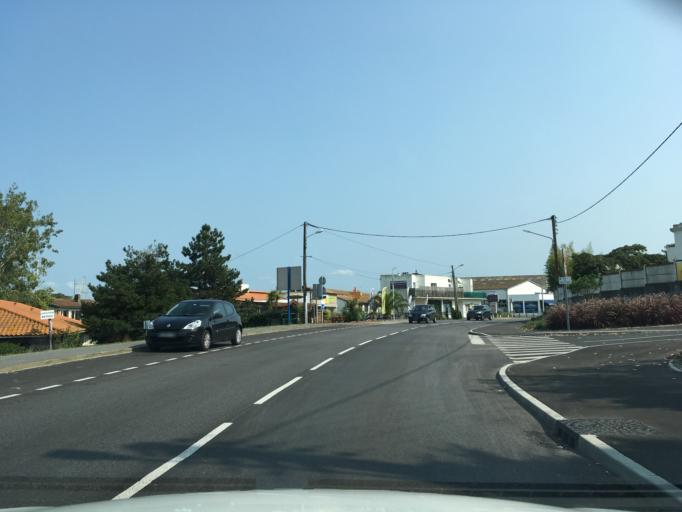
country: FR
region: Aquitaine
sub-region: Departement des Pyrenees-Atlantiques
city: Boucau
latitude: 43.5244
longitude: -1.5051
